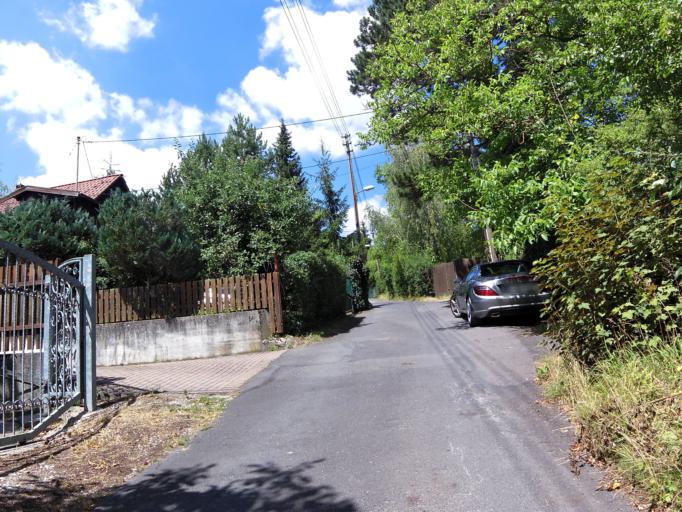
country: DE
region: Bavaria
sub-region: Regierungsbezirk Unterfranken
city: Hochberg
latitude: 49.7741
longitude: 9.9044
